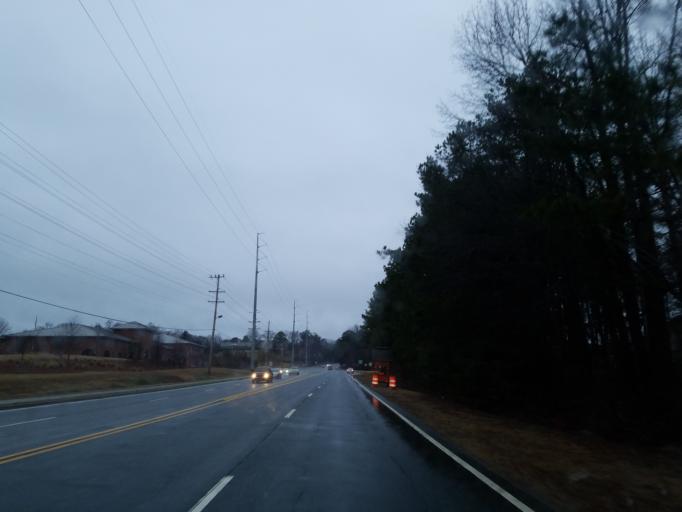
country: US
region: Georgia
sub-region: Gwinnett County
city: Norcross
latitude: 33.9758
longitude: -84.2642
